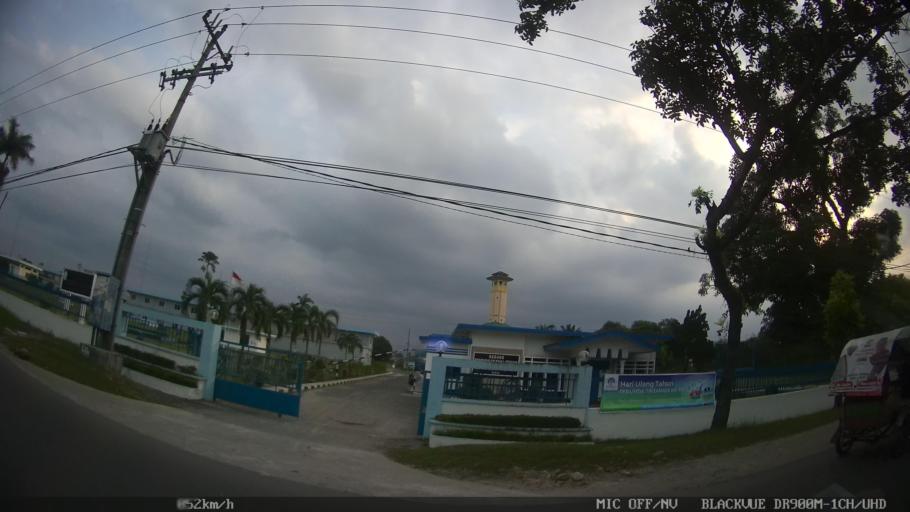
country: ID
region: North Sumatra
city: Sunggal
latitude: 3.5696
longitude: 98.6111
